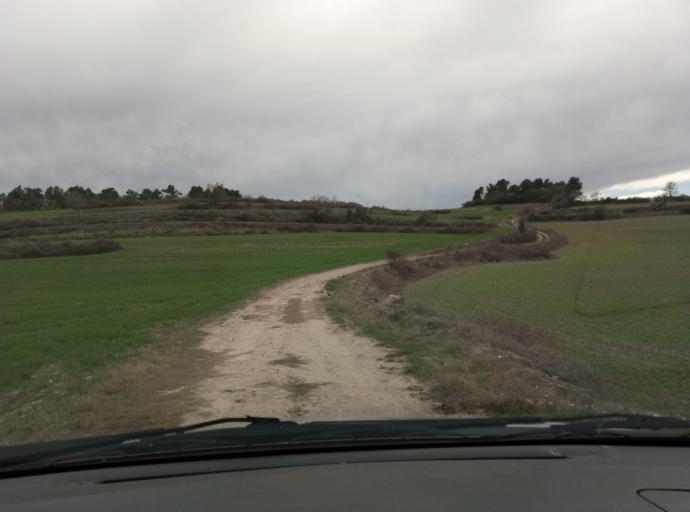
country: ES
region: Catalonia
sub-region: Provincia de Lleida
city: Ciutadilla
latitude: 41.5182
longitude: 1.1606
